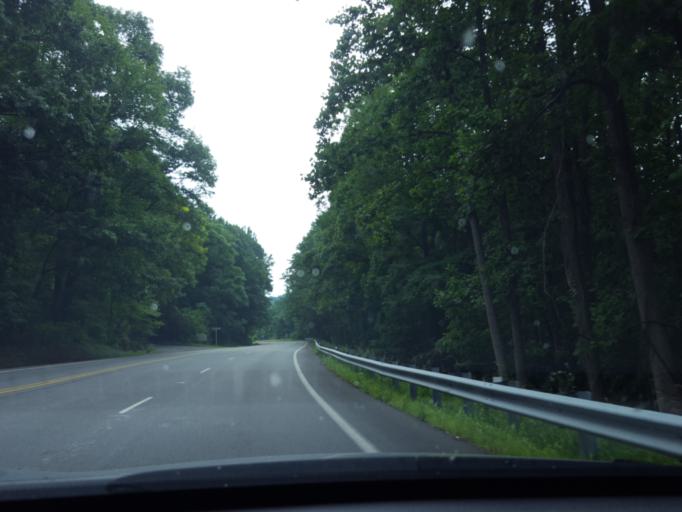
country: US
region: Virginia
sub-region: City of Waynesboro
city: Waynesboro
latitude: 38.0398
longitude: -78.8581
